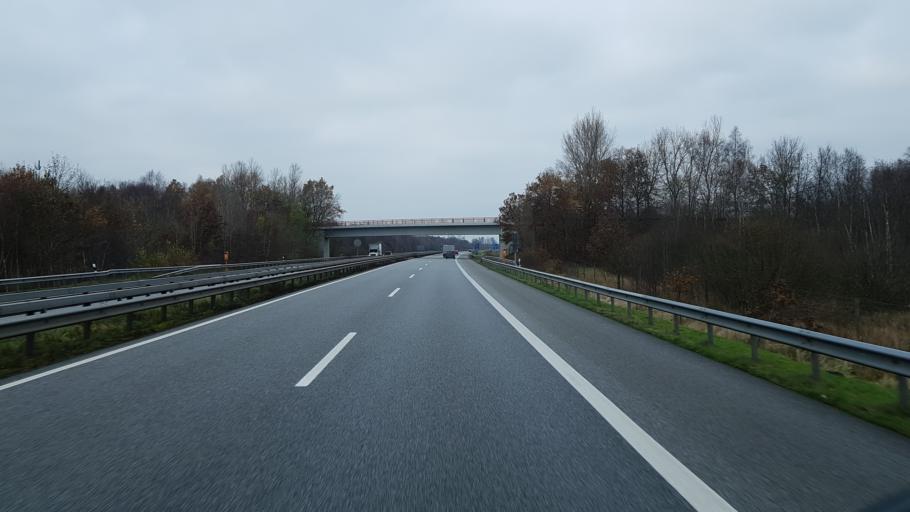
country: DE
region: Lower Saxony
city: Driftsethe
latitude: 53.3619
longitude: 8.5830
